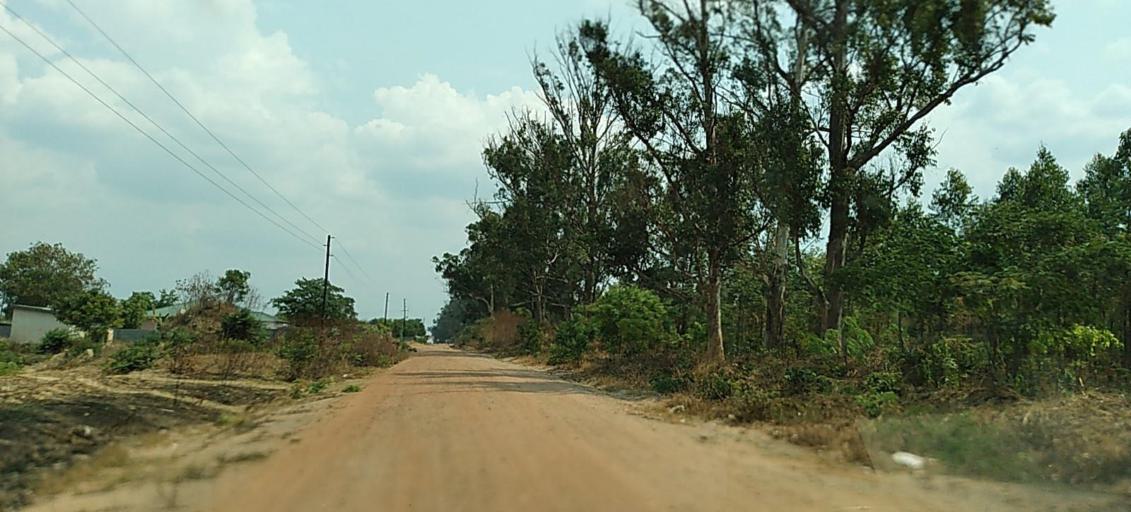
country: ZM
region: Copperbelt
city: Kalulushi
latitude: -12.8391
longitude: 28.0777
